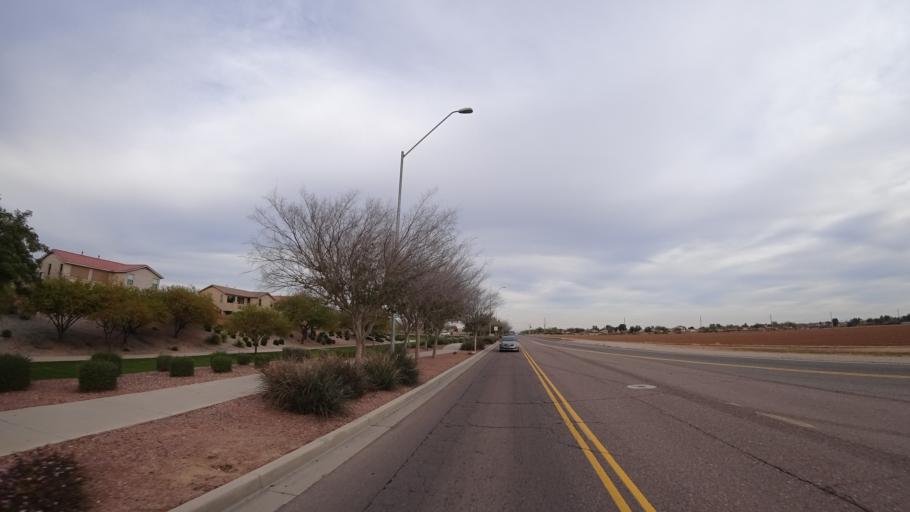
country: US
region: Arizona
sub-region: Maricopa County
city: Surprise
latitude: 33.6243
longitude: -112.4136
